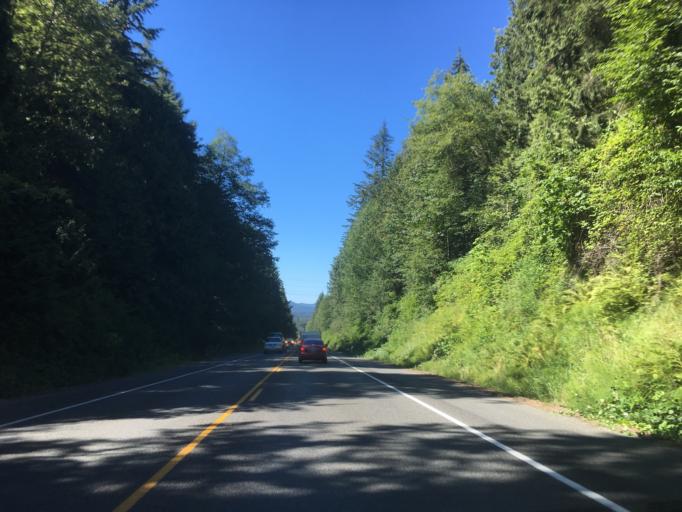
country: US
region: Washington
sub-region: Snohomish County
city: Arlington
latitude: 48.1690
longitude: -122.1213
